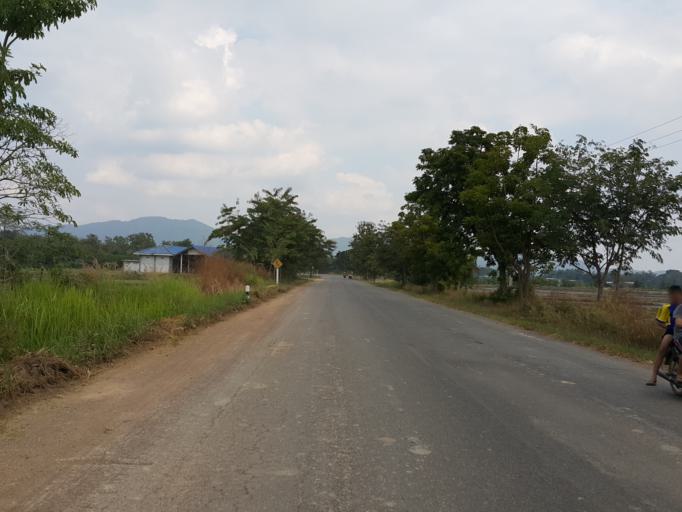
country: TH
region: Sukhothai
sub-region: Amphoe Si Satchanalai
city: Si Satchanalai
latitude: 17.4664
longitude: 99.6379
